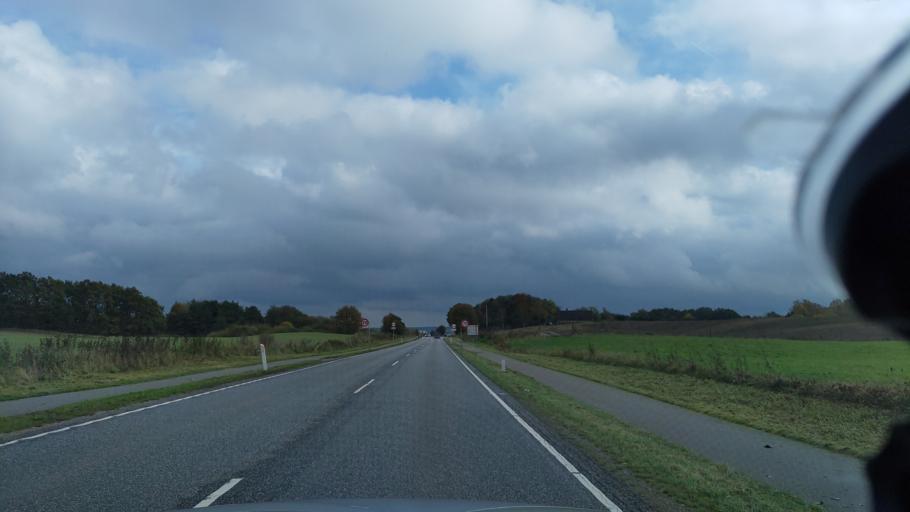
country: DK
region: Zealand
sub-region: Faxe Kommune
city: Haslev
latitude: 55.2633
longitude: 11.9528
